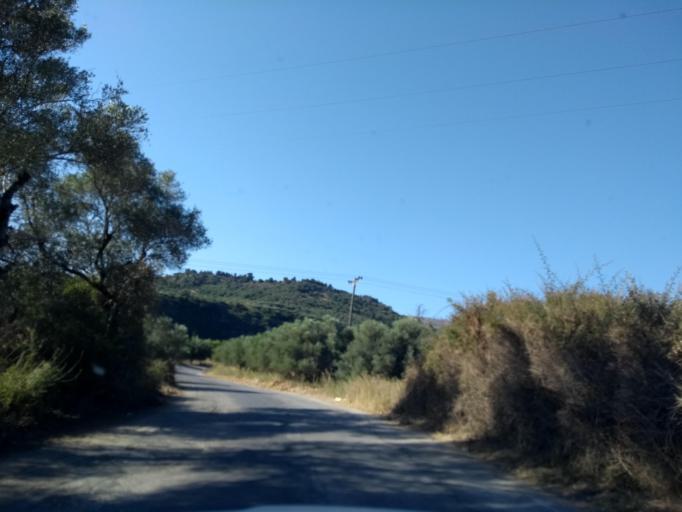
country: GR
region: Crete
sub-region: Nomos Chanias
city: Georgioupolis
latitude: 35.3666
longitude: 24.2281
